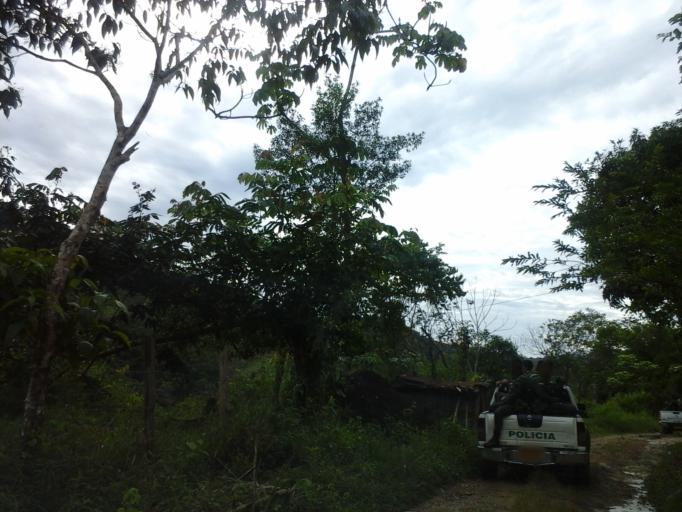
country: CO
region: Antioquia
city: San Roque
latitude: 6.4967
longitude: -74.9694
